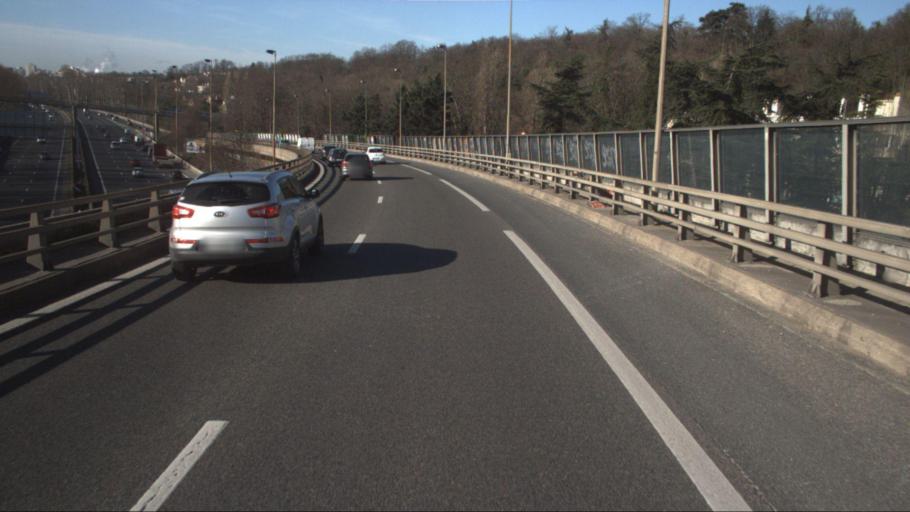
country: FR
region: Ile-de-France
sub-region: Departement du Val-de-Marne
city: Maisons-Alfort
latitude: 48.8169
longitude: 2.4460
